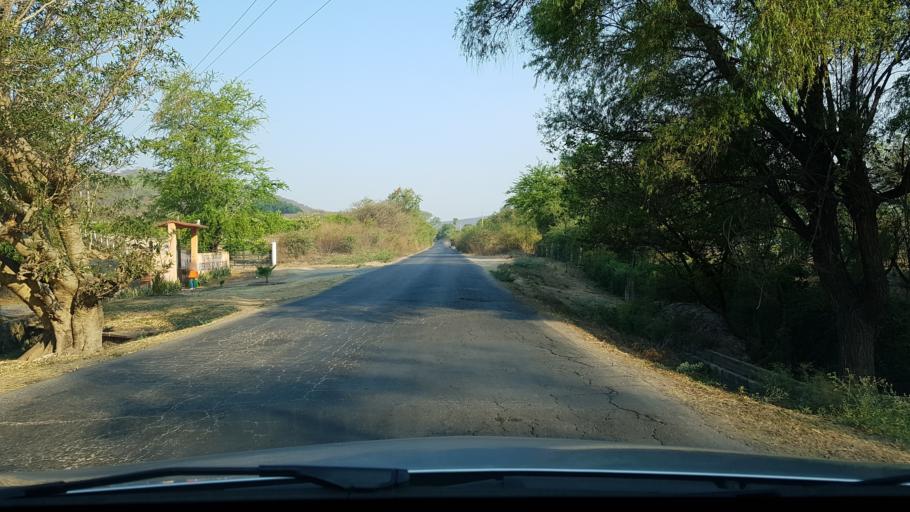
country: MX
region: Morelos
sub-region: Tepalcingo
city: Zacapalco
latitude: 18.6454
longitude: -99.0230
